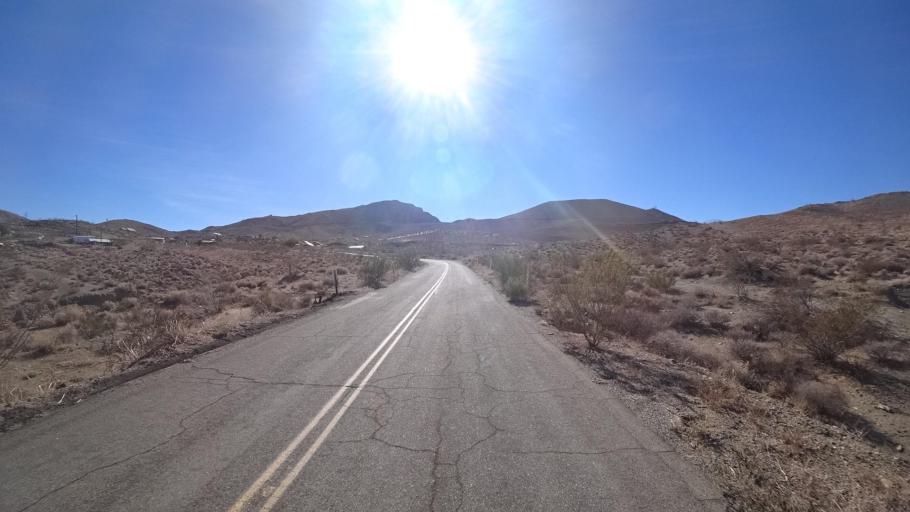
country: US
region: California
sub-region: Kern County
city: Ridgecrest
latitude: 35.3708
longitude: -117.6598
